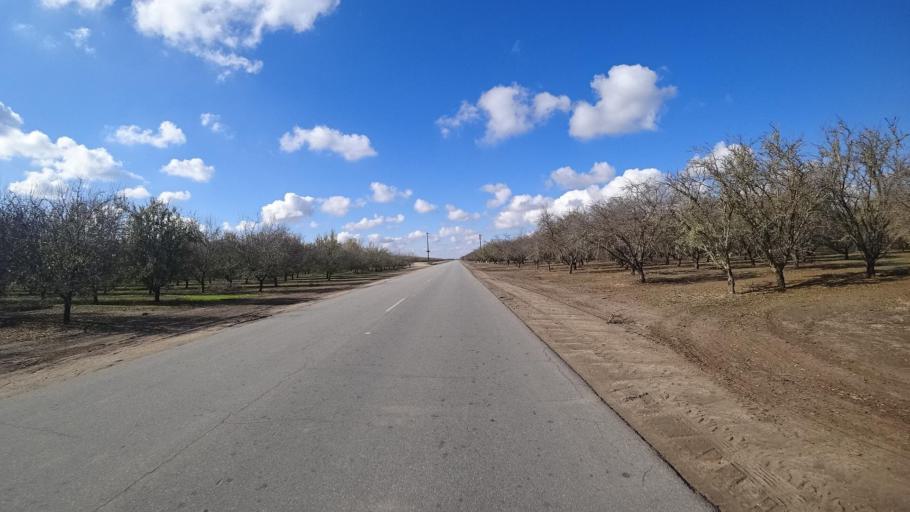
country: US
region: California
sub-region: Kern County
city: McFarland
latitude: 35.6742
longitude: -119.3018
